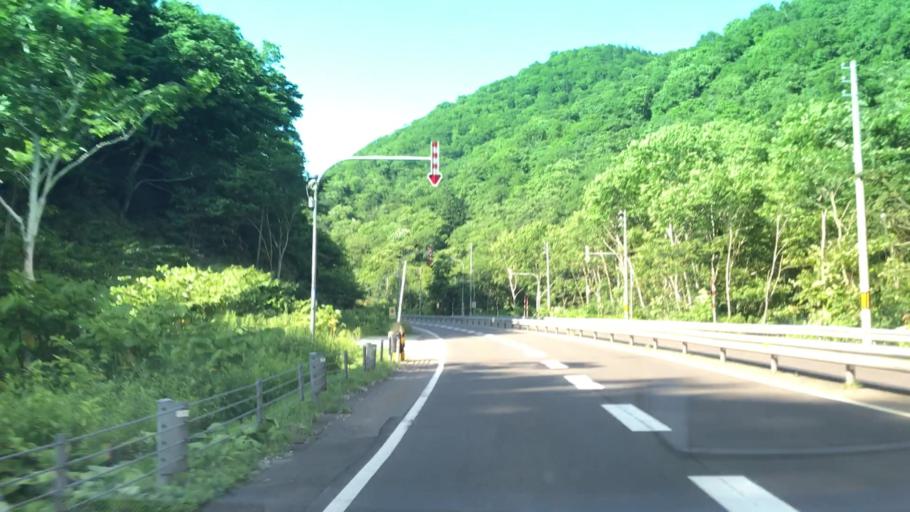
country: JP
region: Hokkaido
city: Yoichi
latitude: 43.0427
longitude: 140.6807
